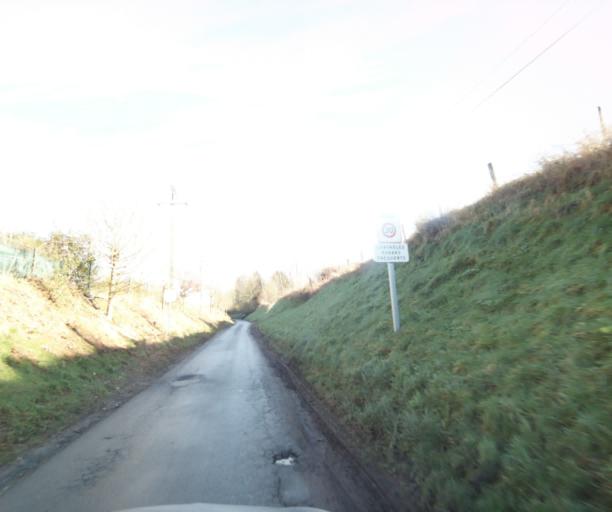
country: FR
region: Nord-Pas-de-Calais
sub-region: Departement du Nord
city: Aulnoy-lez-Valenciennes
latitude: 50.3290
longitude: 3.5377
